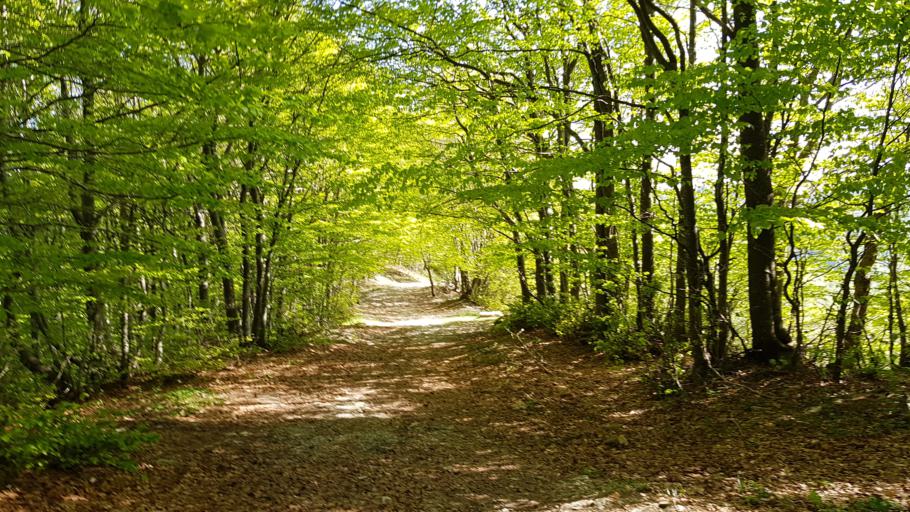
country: IT
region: Liguria
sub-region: Provincia di Genova
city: Fascia
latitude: 44.6058
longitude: 9.2042
